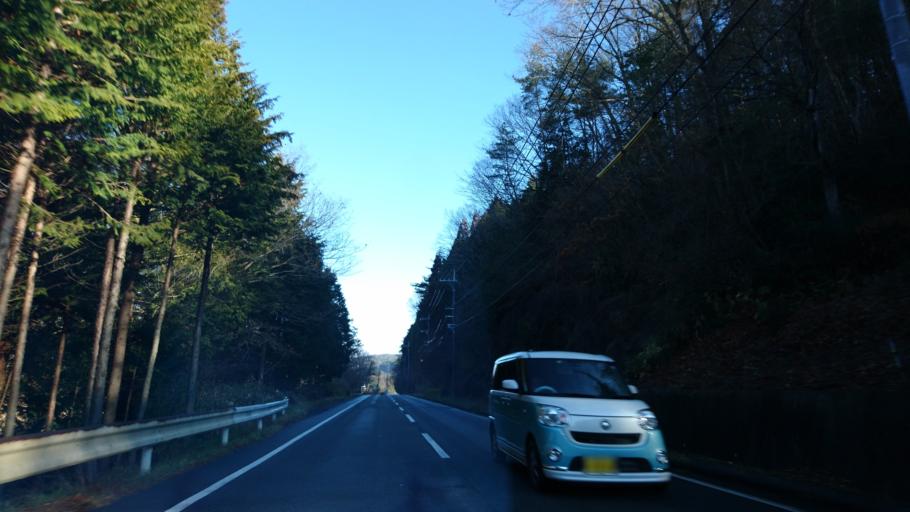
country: JP
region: Okayama
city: Takahashi
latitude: 34.8078
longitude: 133.6724
